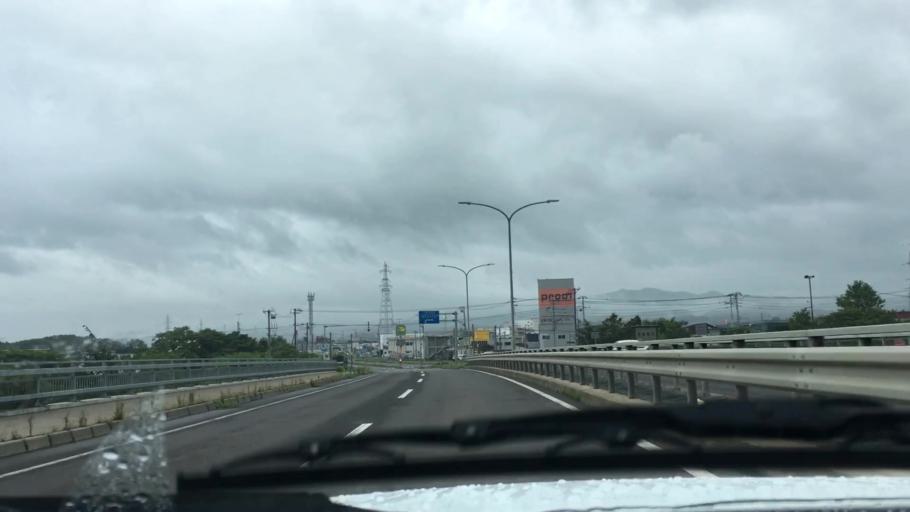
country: JP
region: Hokkaido
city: Nanae
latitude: 42.2627
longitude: 140.2738
